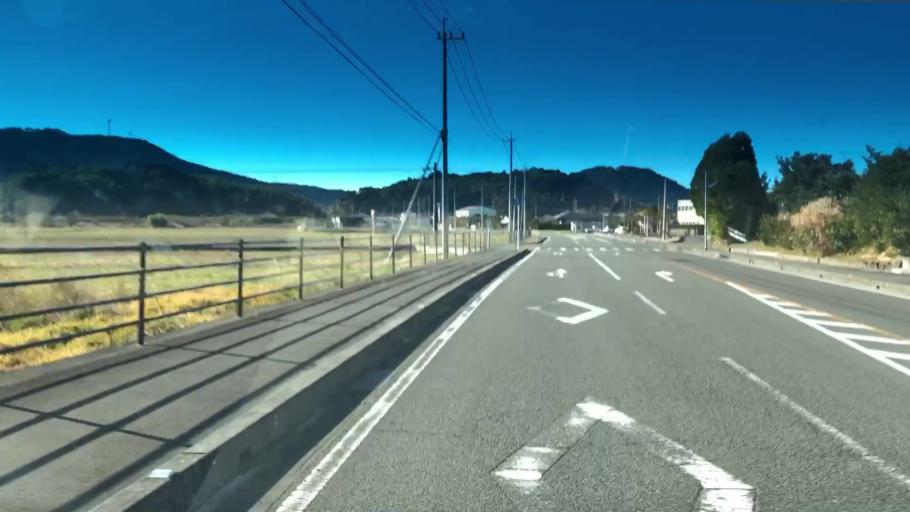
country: JP
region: Kagoshima
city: Satsumasendai
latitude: 31.8168
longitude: 130.2832
